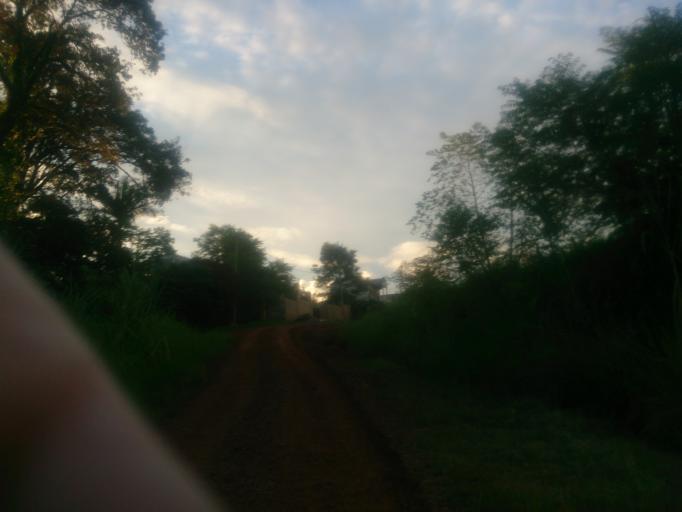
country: AR
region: Misiones
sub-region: Departamento de Obera
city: Obera
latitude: -27.4775
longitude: -55.1044
